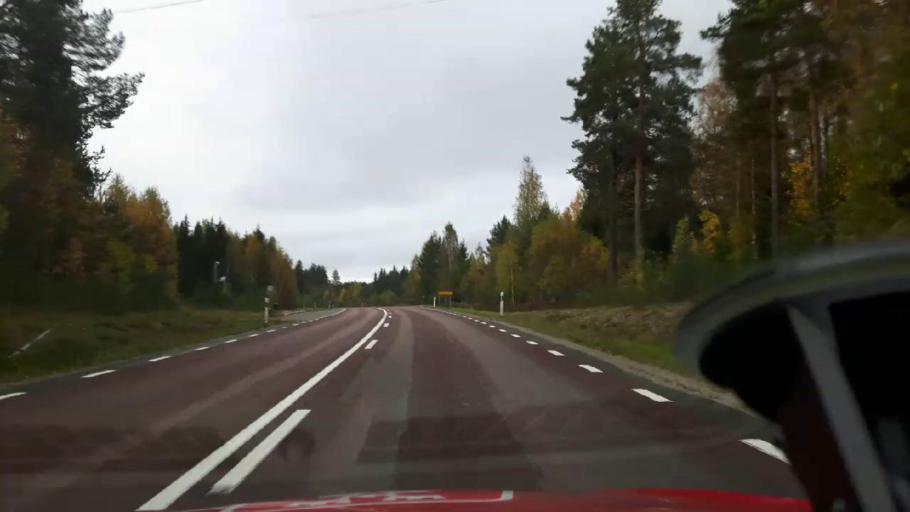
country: SE
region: Jaemtland
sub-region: Harjedalens Kommun
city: Sveg
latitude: 62.2703
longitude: 14.8038
